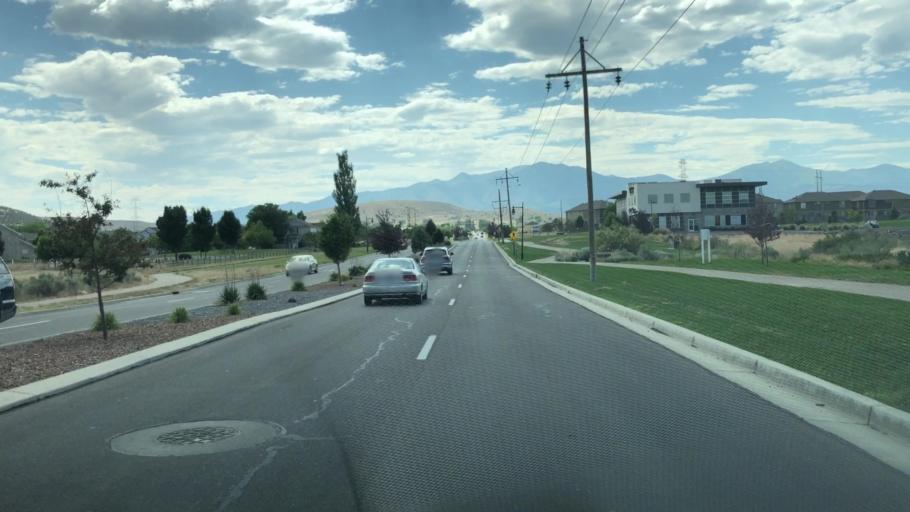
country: US
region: Utah
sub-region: Utah County
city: Eagle Mountain
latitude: 40.3622
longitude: -111.9665
